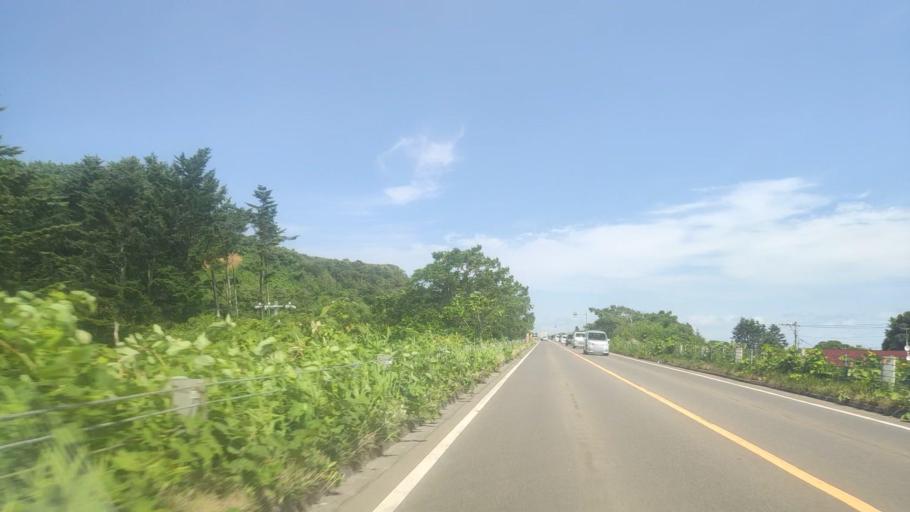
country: JP
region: Hokkaido
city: Nanae
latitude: 42.1937
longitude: 140.4199
